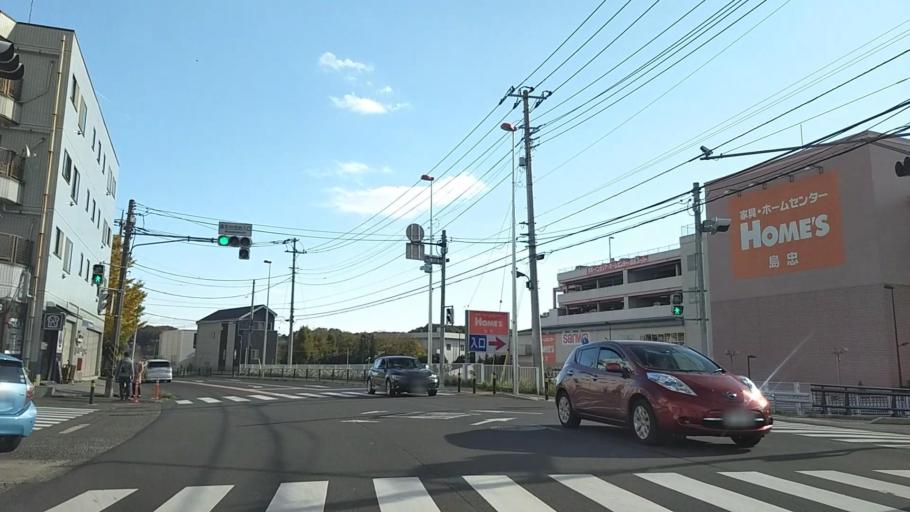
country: JP
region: Tokyo
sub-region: Machida-shi
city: Machida
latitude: 35.5797
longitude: 139.5007
